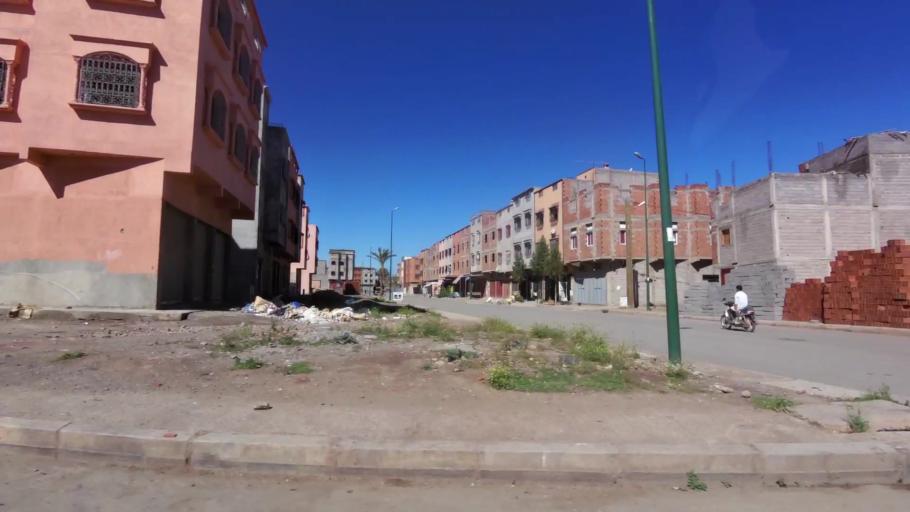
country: MA
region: Marrakech-Tensift-Al Haouz
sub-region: Marrakech
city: Marrakesh
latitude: 31.5901
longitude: -8.0560
